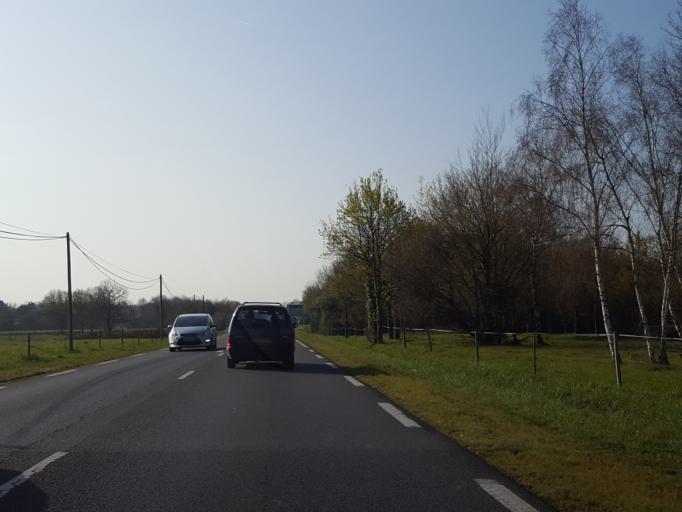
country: FR
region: Pays de la Loire
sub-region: Departement de la Loire-Atlantique
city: Le Bignon
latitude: 47.0941
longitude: -1.5311
